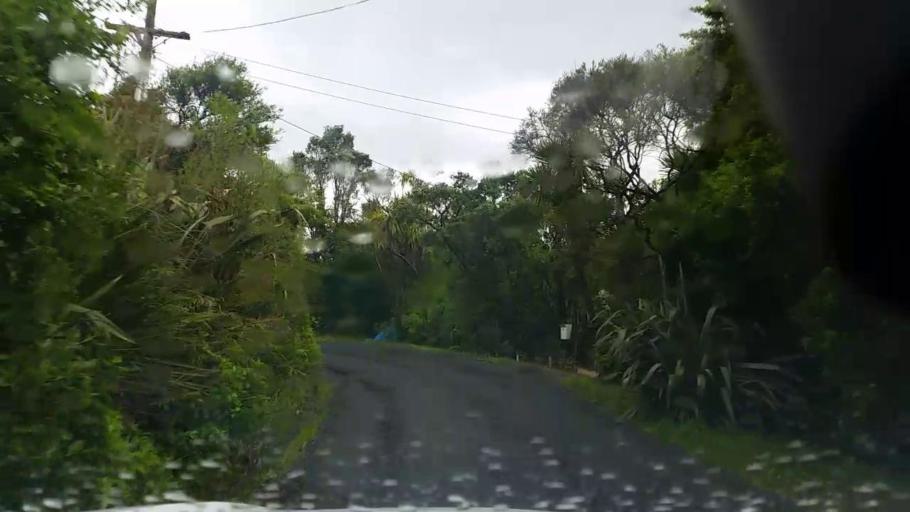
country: NZ
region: Auckland
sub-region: Auckland
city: Muriwai Beach
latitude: -36.9342
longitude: 174.5046
